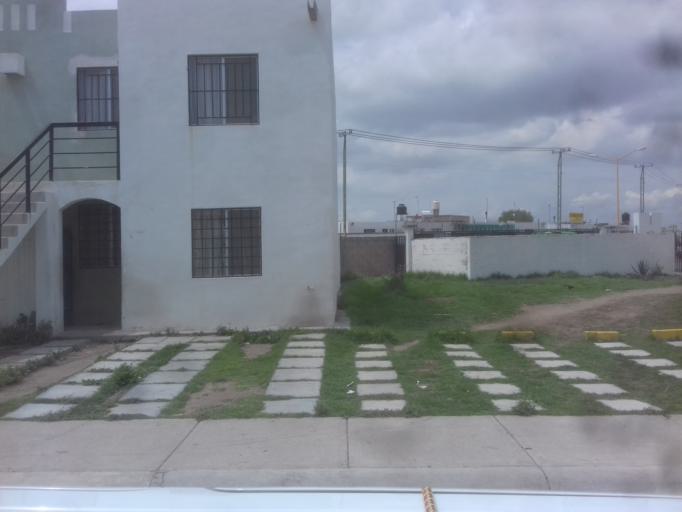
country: MX
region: Aguascalientes
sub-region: Aguascalientes
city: San Sebastian [Fraccionamiento]
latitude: 21.8070
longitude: -102.2685
